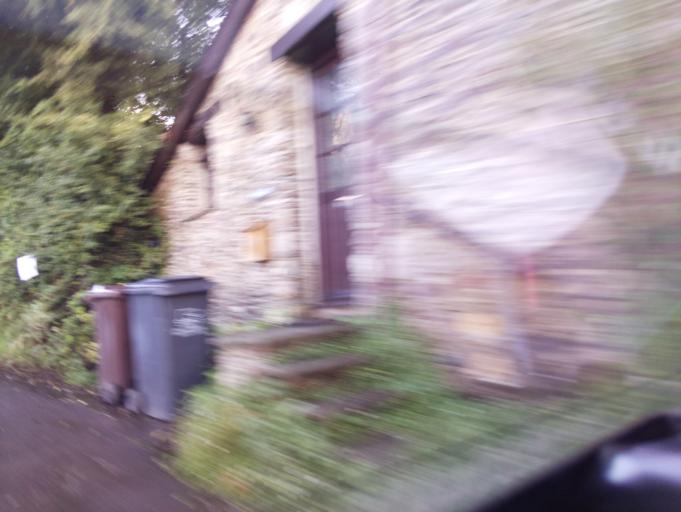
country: GB
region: England
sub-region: Devon
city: Totnes
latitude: 50.3456
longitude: -3.6912
